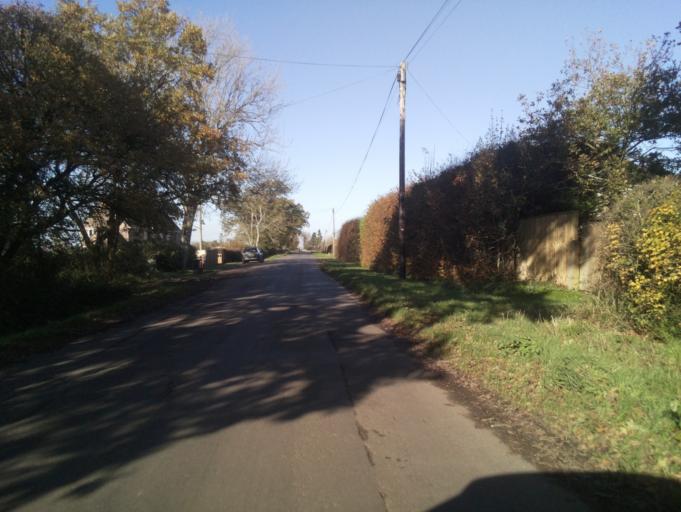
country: GB
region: England
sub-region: Dorset
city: Sherborne
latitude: 50.8725
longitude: -2.5273
